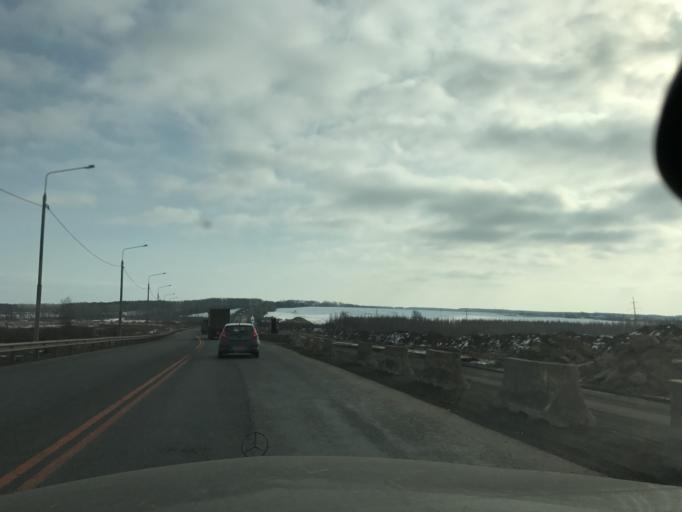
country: RU
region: Vladimir
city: Novovyazniki
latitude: 56.2173
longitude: 42.2258
